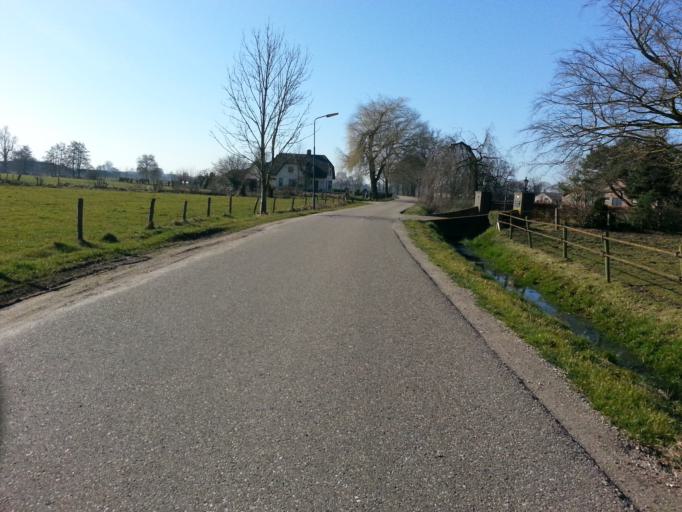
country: NL
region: Utrecht
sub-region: Gemeente Woudenberg
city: Woudenberg
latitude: 52.0753
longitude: 5.4347
